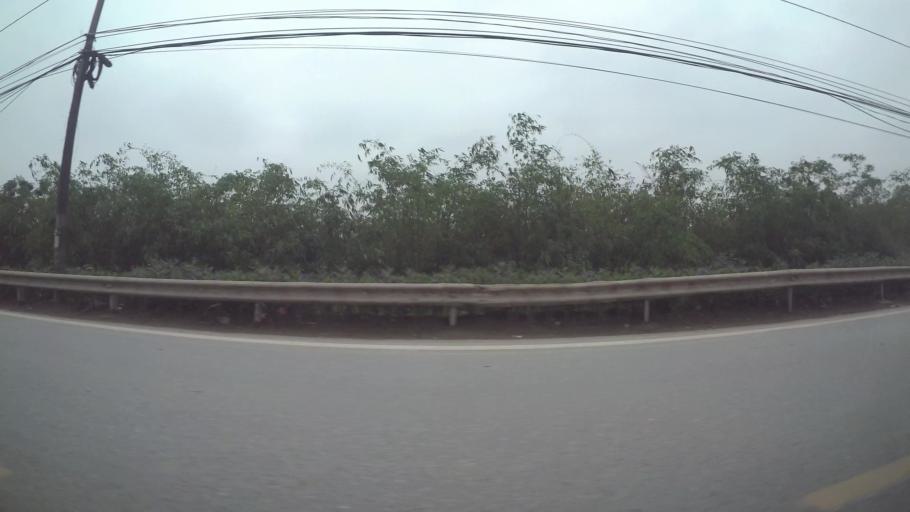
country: VN
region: Hung Yen
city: Van Giang
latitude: 20.9834
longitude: 105.8950
